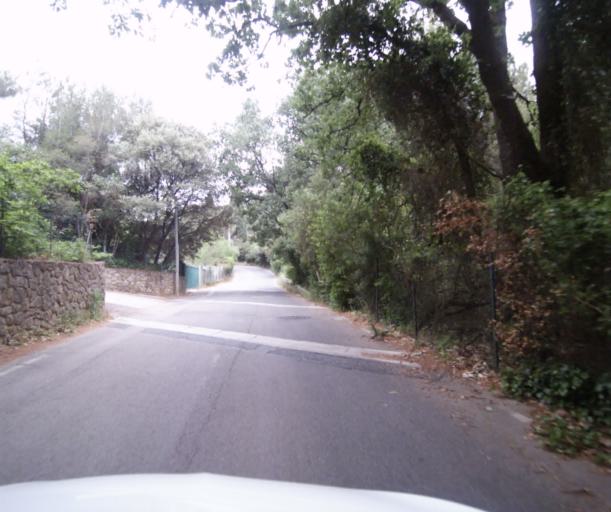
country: FR
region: Provence-Alpes-Cote d'Azur
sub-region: Departement du Var
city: Ollioules
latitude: 43.1463
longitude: 5.8822
